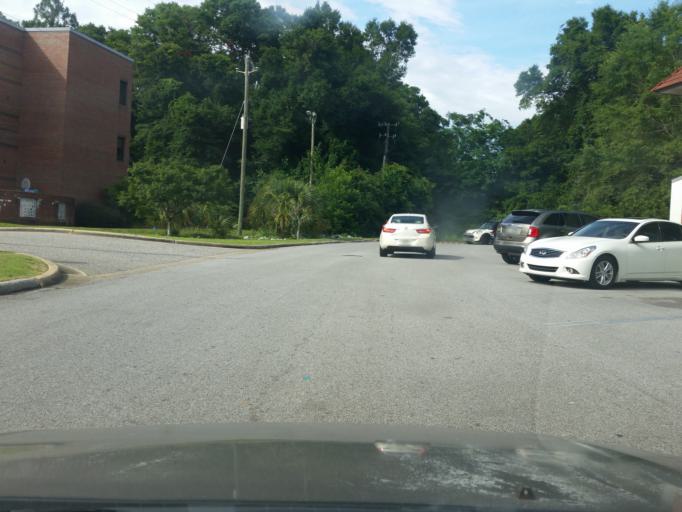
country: US
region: Florida
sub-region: Escambia County
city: Brent
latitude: 30.4765
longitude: -87.2151
